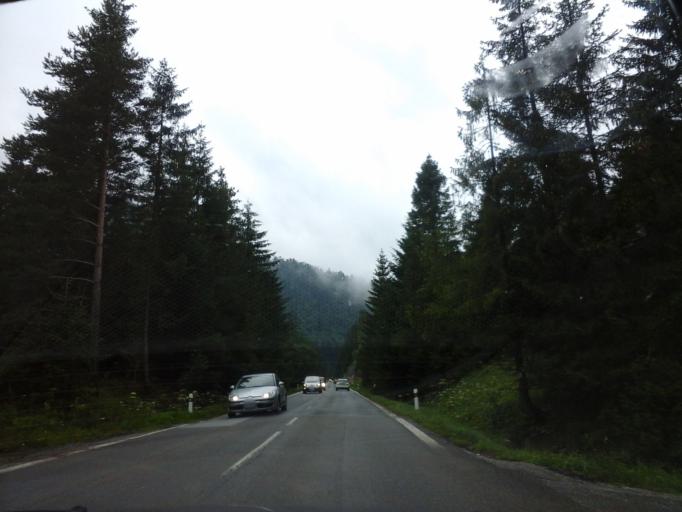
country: SK
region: Presovsky
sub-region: Okres Poprad
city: Zdiar
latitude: 49.2504
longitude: 20.3085
